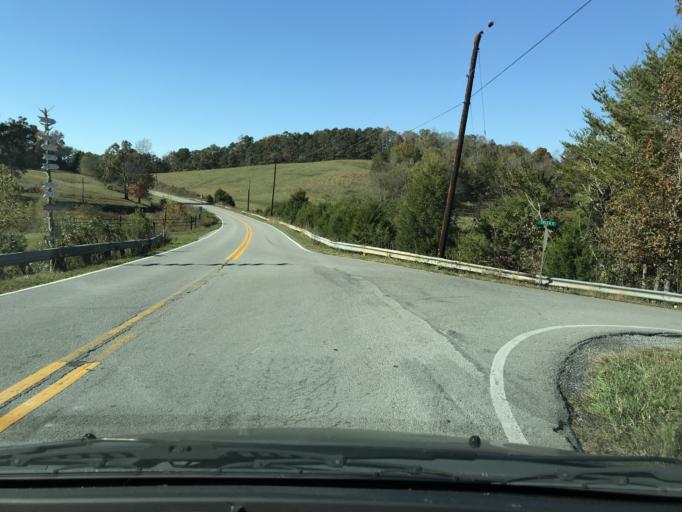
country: US
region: Georgia
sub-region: Dade County
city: Trenton
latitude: 34.8820
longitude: -85.4719
